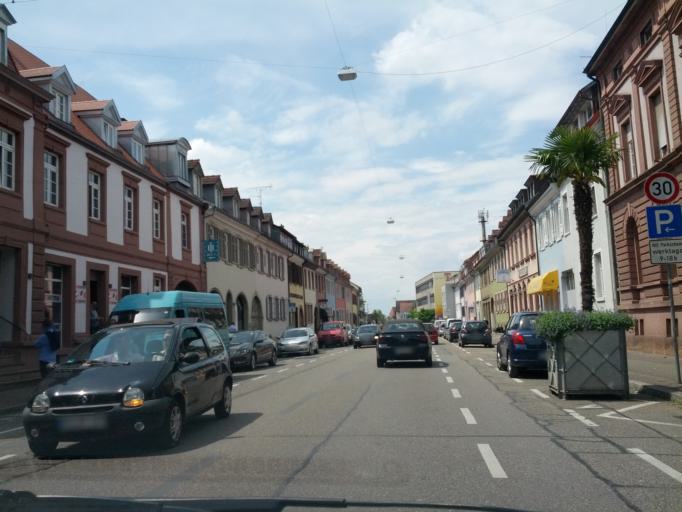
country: DE
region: Baden-Wuerttemberg
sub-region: Freiburg Region
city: Emmendingen
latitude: 48.1225
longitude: 7.8456
